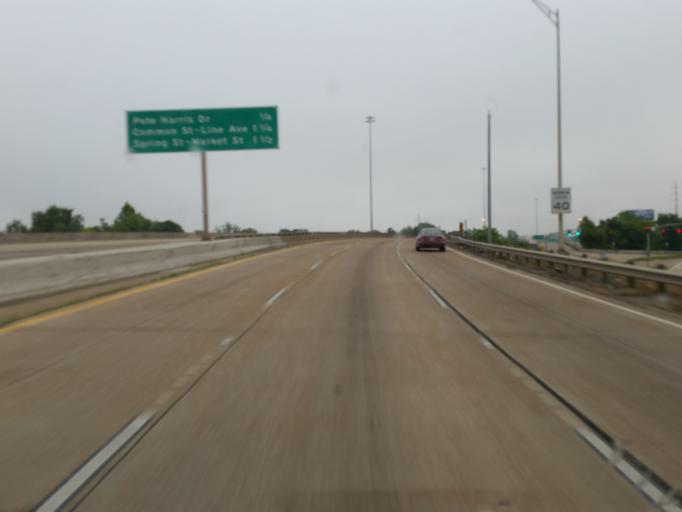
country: US
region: Louisiana
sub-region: Caddo Parish
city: Shreveport
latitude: 32.4913
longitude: -93.7712
